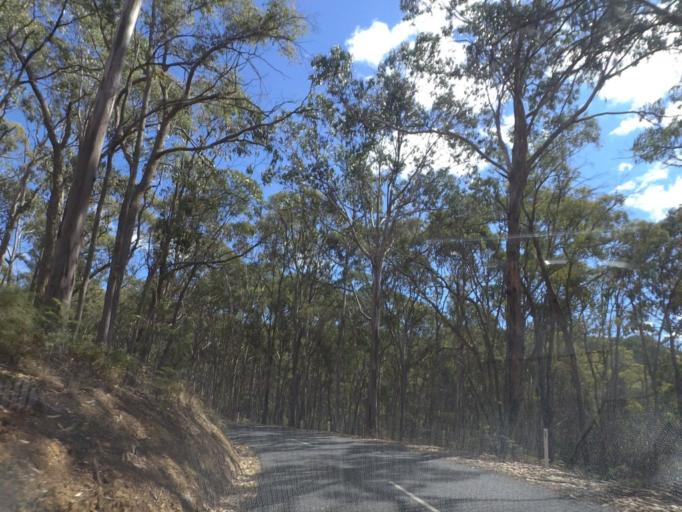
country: AU
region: Victoria
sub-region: Murrindindi
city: Alexandra
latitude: -37.3368
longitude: 145.9639
